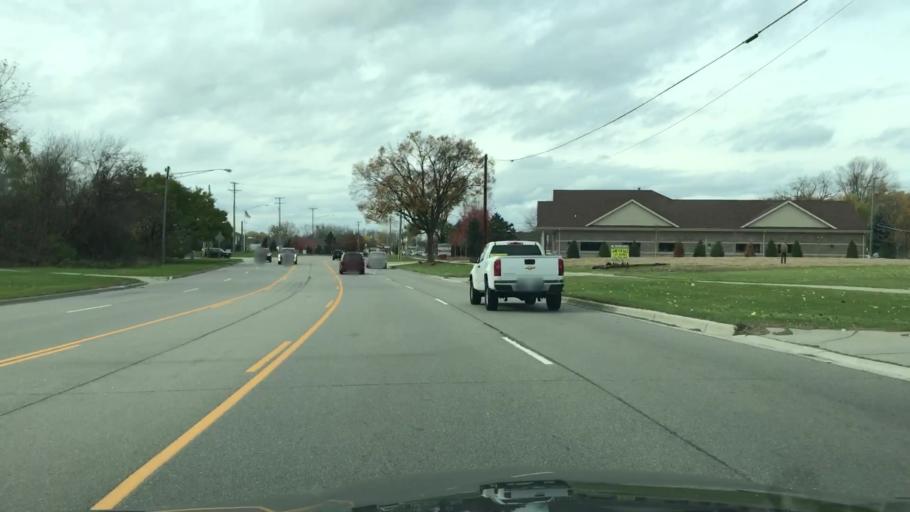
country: US
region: Michigan
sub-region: Macomb County
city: Sterling Heights
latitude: 42.5500
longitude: -83.0821
